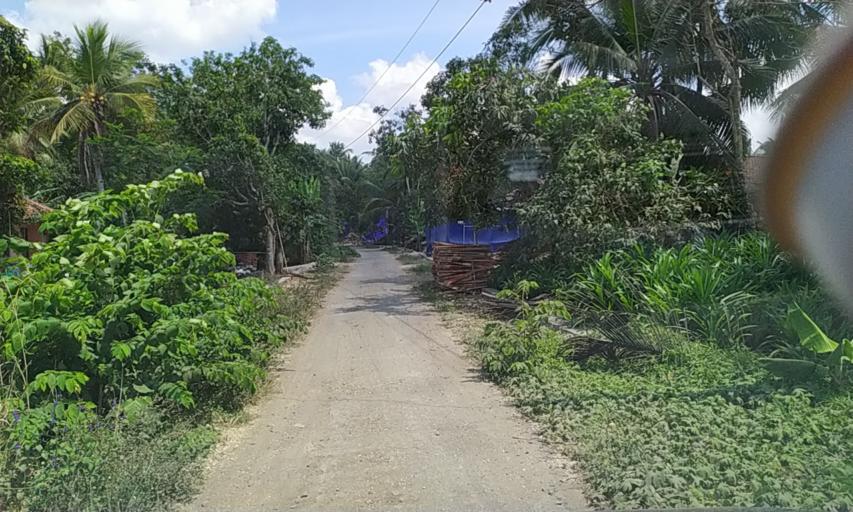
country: ID
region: Central Java
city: Cimrutu
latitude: -7.6054
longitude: 108.7894
